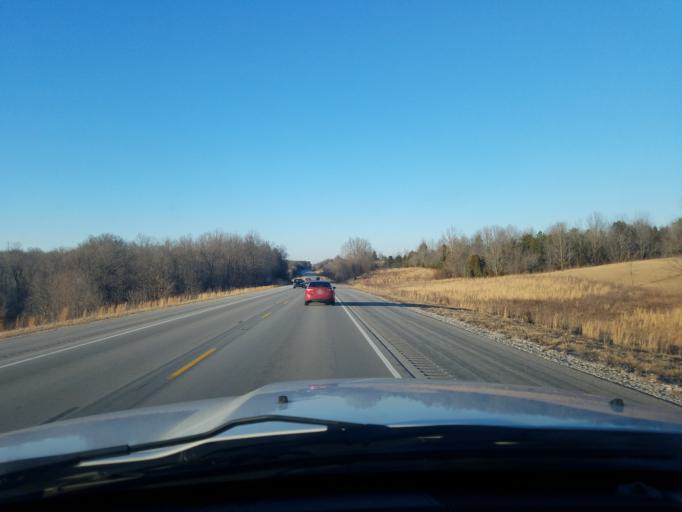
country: US
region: Indiana
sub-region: Crawford County
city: English
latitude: 38.1394
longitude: -86.6049
